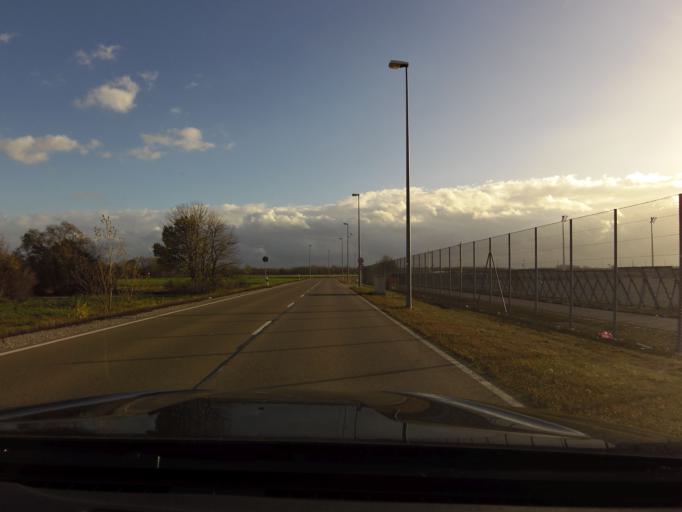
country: DE
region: Bavaria
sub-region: Upper Bavaria
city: Oberding
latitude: 48.3528
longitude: 11.8071
